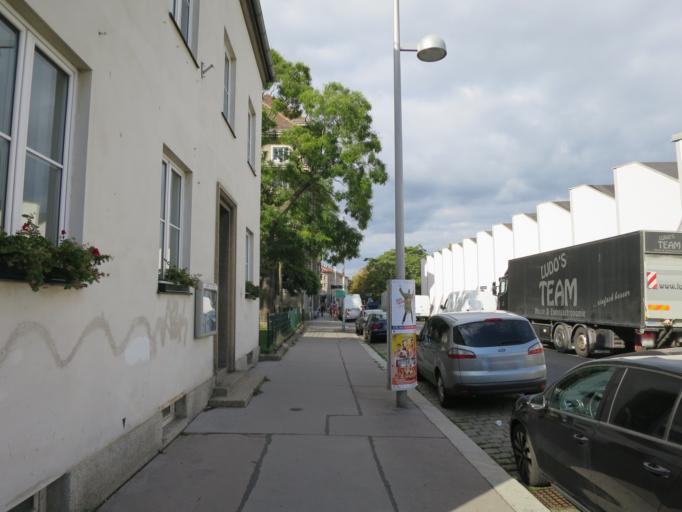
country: AT
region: Vienna
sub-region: Wien Stadt
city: Vienna
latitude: 48.2025
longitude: 16.3314
